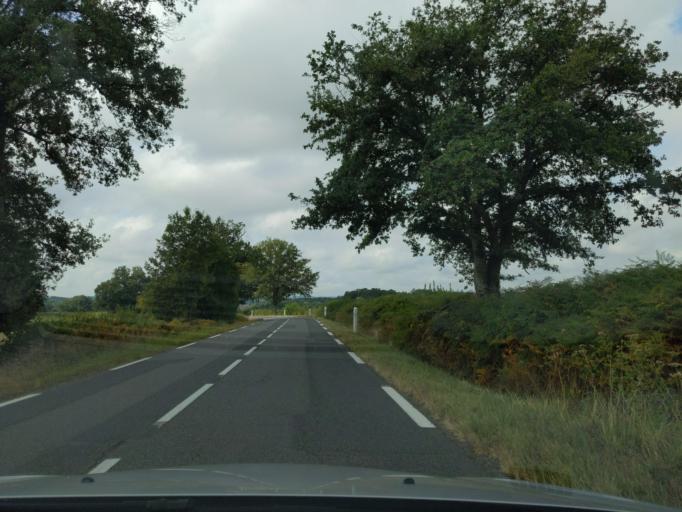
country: FR
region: Bourgogne
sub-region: Departement de la Nievre
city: Luzy
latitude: 46.7564
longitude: 3.9385
